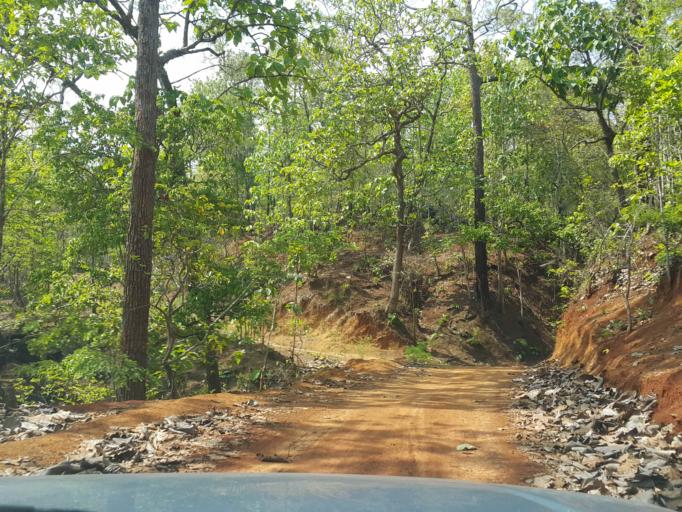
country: TH
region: Chiang Mai
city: Wiang Haeng
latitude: 19.3258
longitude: 98.7205
